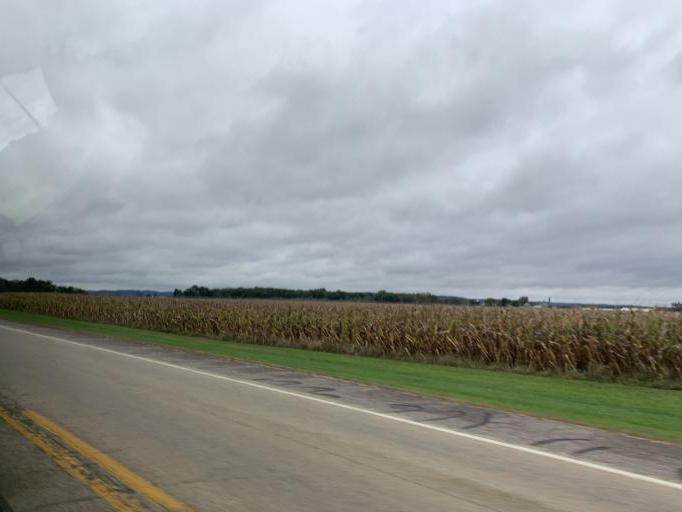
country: US
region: Wisconsin
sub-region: Sauk County
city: Prairie du Sac
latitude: 43.2710
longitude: -89.7921
